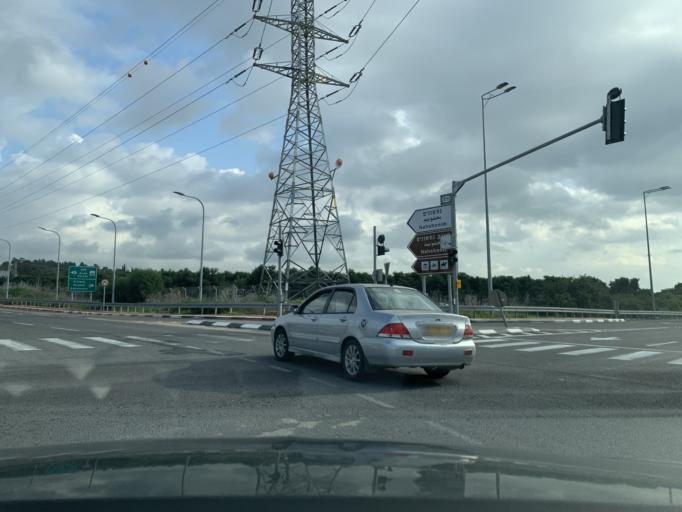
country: IL
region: Central District
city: Rosh Ha'Ayin
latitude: 32.0676
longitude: 34.9440
